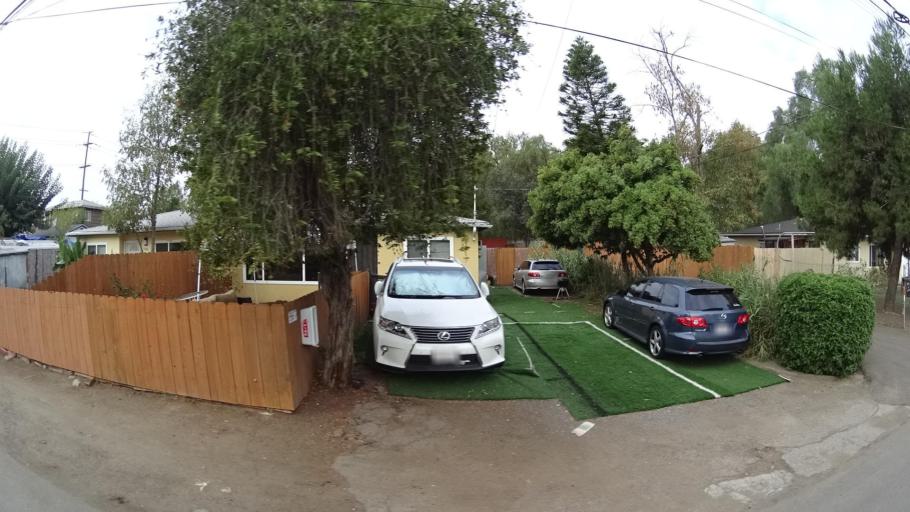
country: US
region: California
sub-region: San Diego County
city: Spring Valley
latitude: 32.7394
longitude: -117.0102
